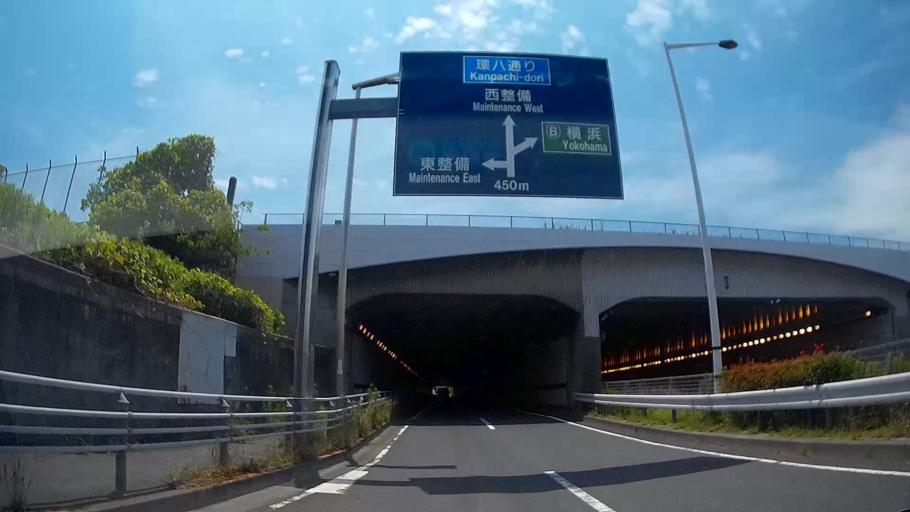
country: JP
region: Kanagawa
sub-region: Kawasaki-shi
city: Kawasaki
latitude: 35.5459
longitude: 139.7900
